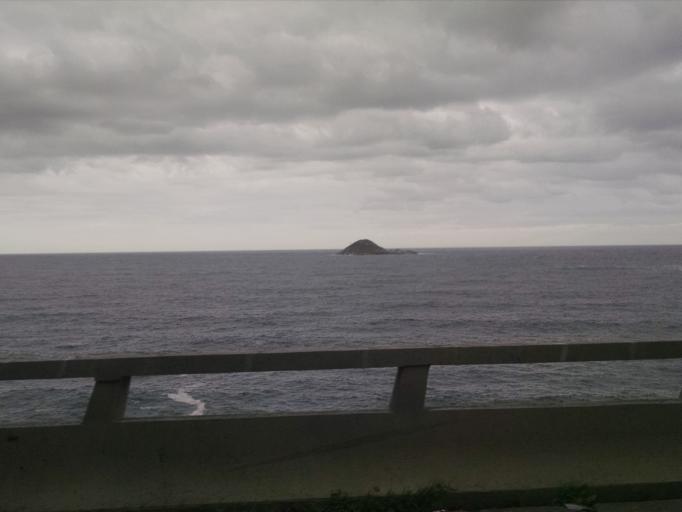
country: BR
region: Rio de Janeiro
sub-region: Rio De Janeiro
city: Rio de Janeiro
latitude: -23.0077
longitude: -43.2844
